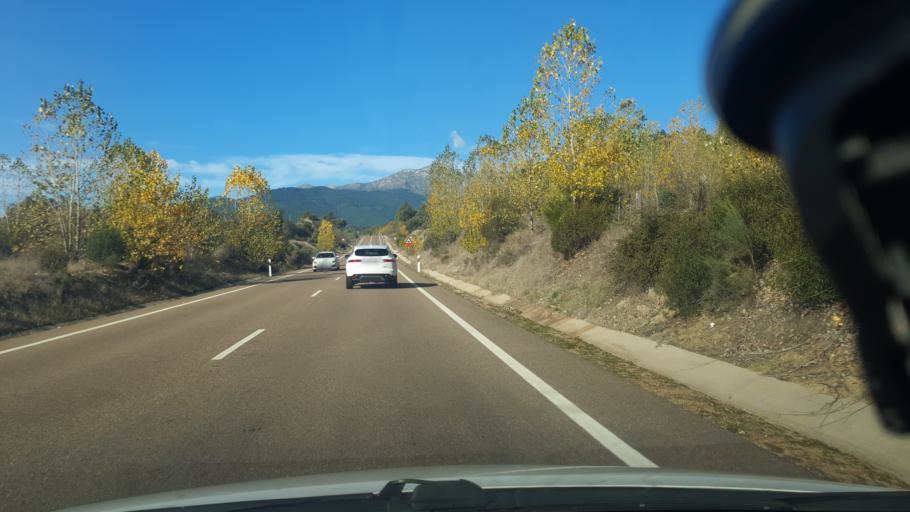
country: ES
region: Castille and Leon
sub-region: Provincia de Avila
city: Arenas de San Pedro
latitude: 40.1882
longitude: -5.0645
